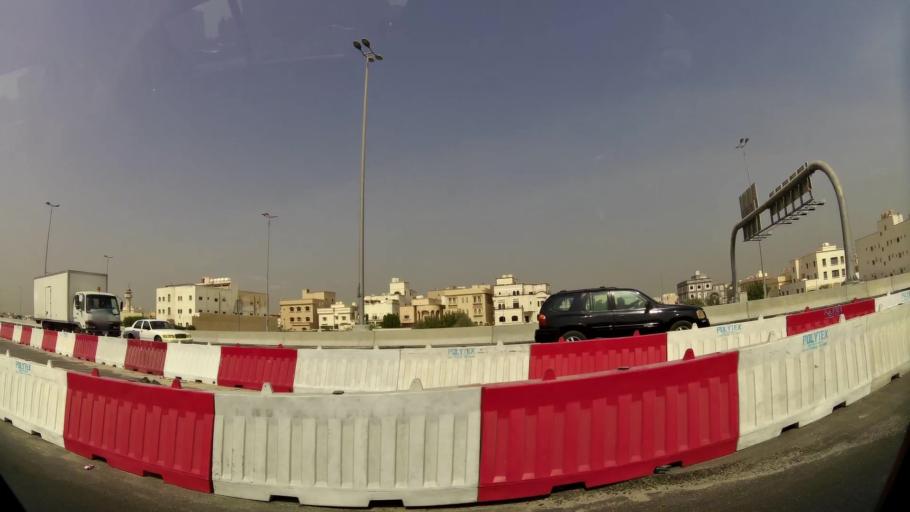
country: KW
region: Al Asimah
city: Ar Rabiyah
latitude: 29.3097
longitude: 47.8746
